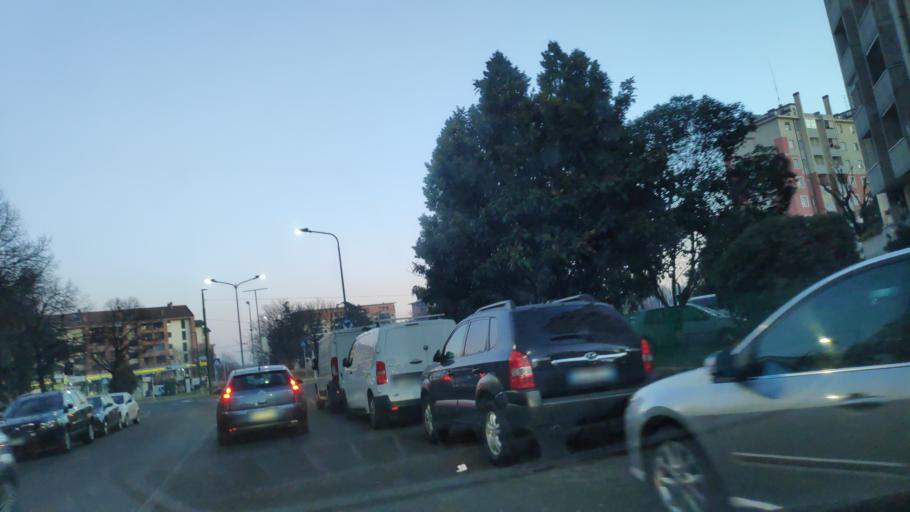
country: IT
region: Lombardy
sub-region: Citta metropolitana di Milano
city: Rozzano
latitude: 45.3826
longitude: 9.1591
